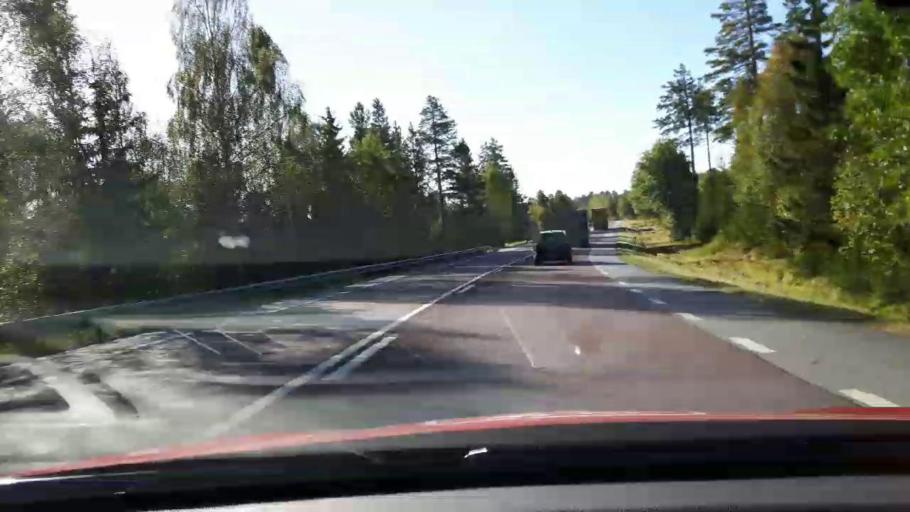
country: SE
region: Jaemtland
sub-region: Braecke Kommun
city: Braecke
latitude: 62.7645
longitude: 15.4083
